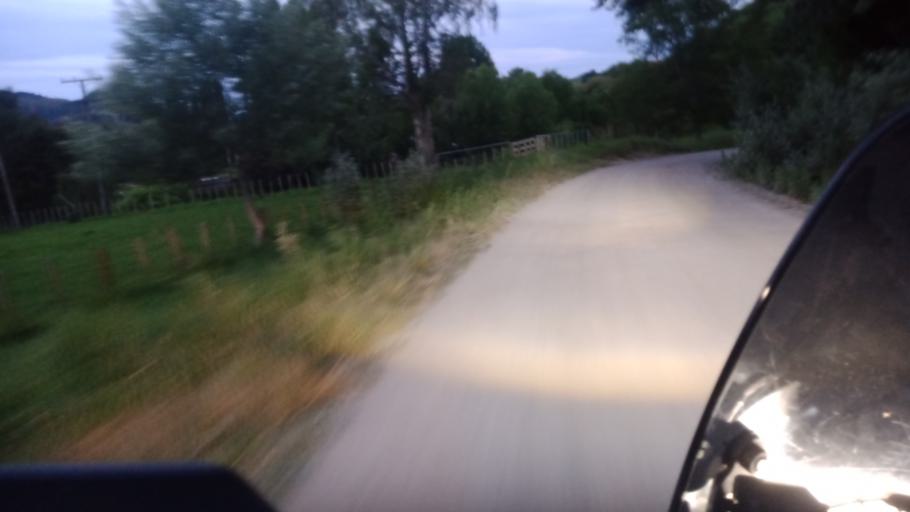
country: NZ
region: Gisborne
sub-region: Gisborne District
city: Gisborne
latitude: -38.4916
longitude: 177.9586
